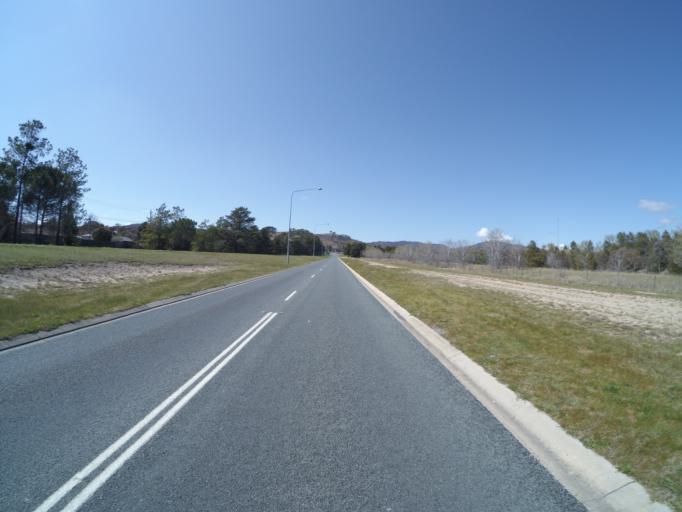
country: AU
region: Australian Capital Territory
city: Macarthur
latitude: -35.4344
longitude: 149.1200
